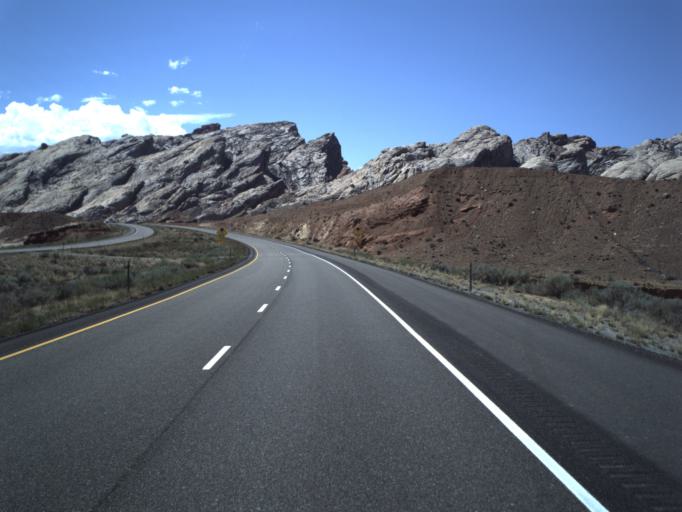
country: US
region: Utah
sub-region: Carbon County
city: East Carbon City
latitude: 38.9251
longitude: -110.4171
